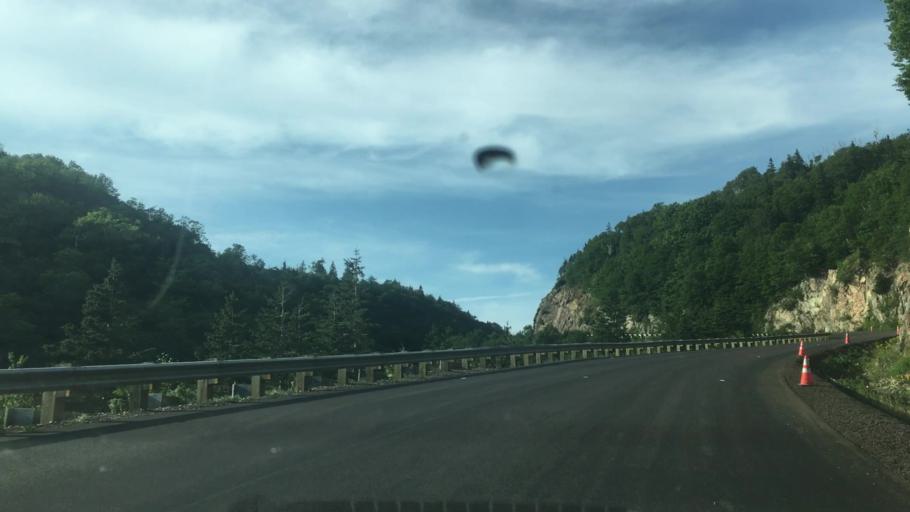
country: CA
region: Nova Scotia
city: Sydney Mines
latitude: 46.8188
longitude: -60.6526
